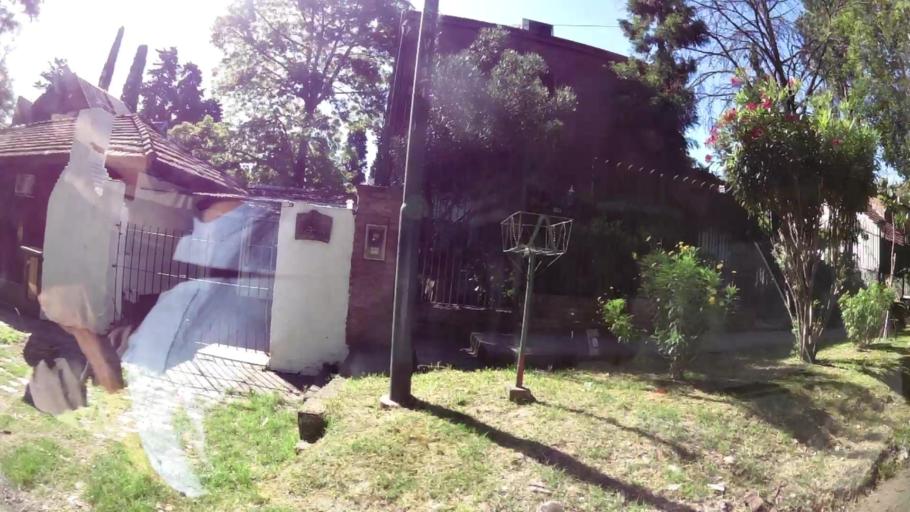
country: AR
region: Buenos Aires
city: Caseros
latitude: -34.5469
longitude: -58.5850
